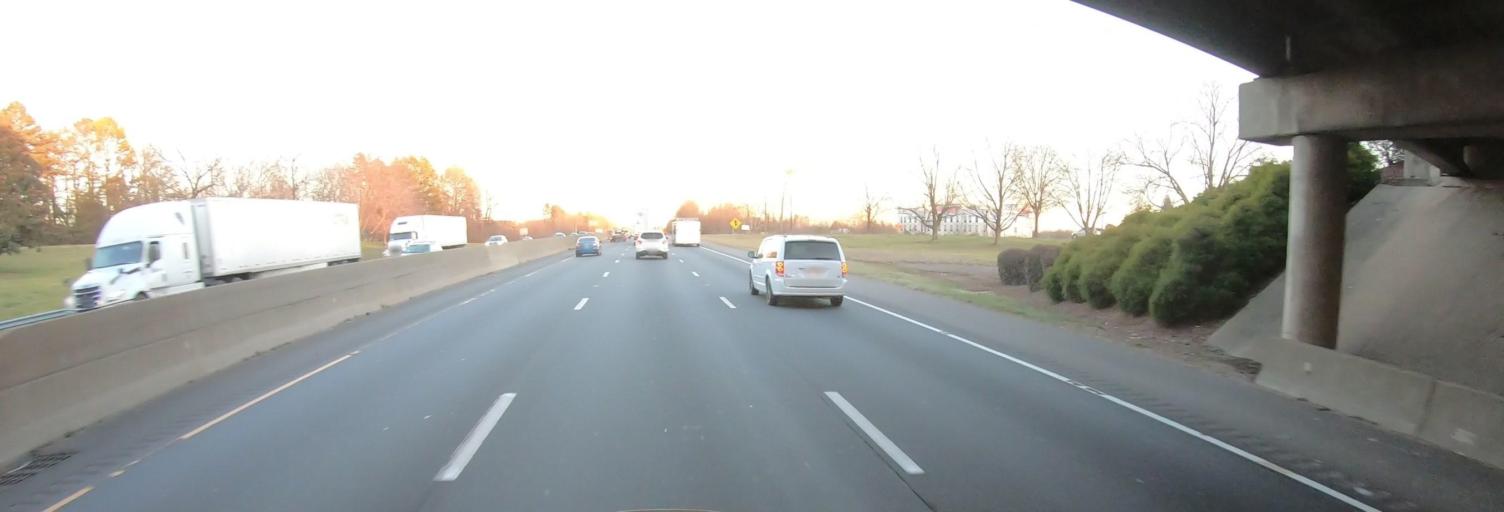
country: US
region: North Carolina
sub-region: Gaston County
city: Ranlo
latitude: 35.2659
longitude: -81.1329
